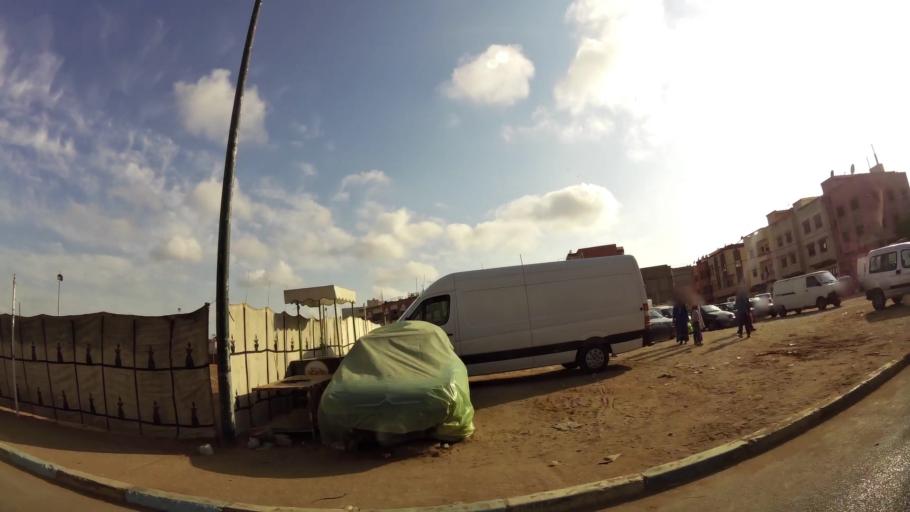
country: MA
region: Rabat-Sale-Zemmour-Zaer
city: Sale
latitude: 34.0502
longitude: -6.7762
